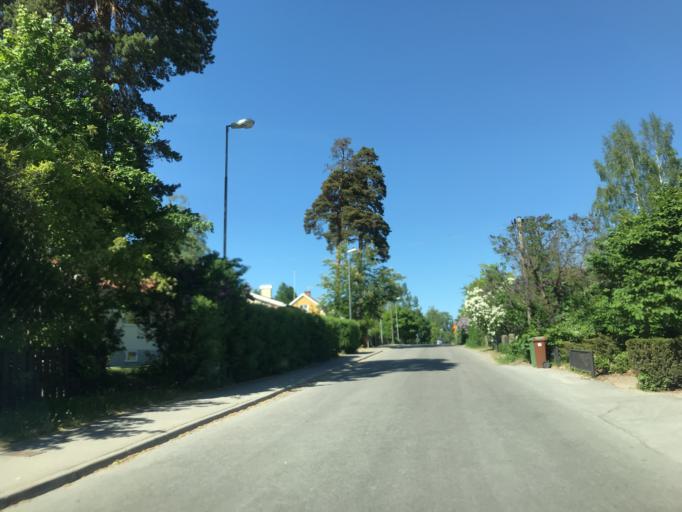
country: SE
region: Stockholm
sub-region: Sollentuna Kommun
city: Sollentuna
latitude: 59.4132
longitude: 17.9730
